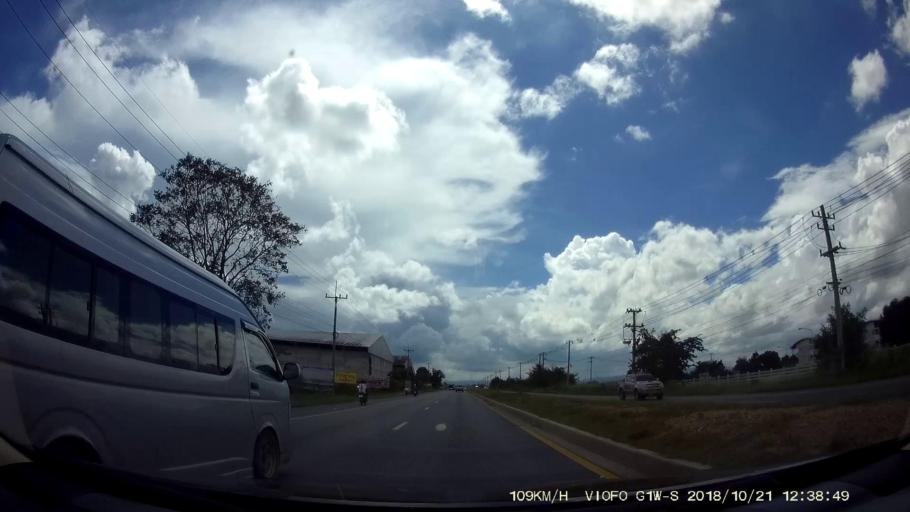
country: TH
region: Nakhon Ratchasima
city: Amphoe Sikhiu
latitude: 15.0482
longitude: 101.7040
